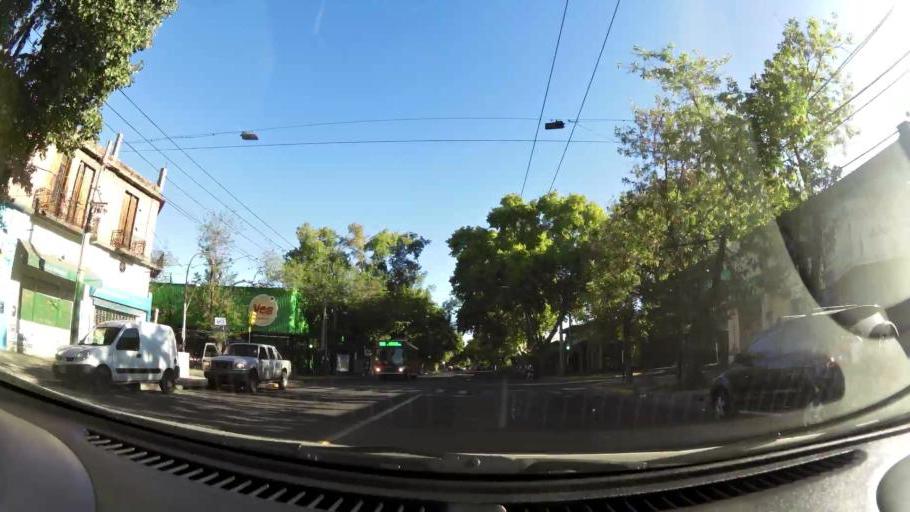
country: AR
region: Mendoza
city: Las Heras
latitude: -32.8703
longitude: -68.8341
